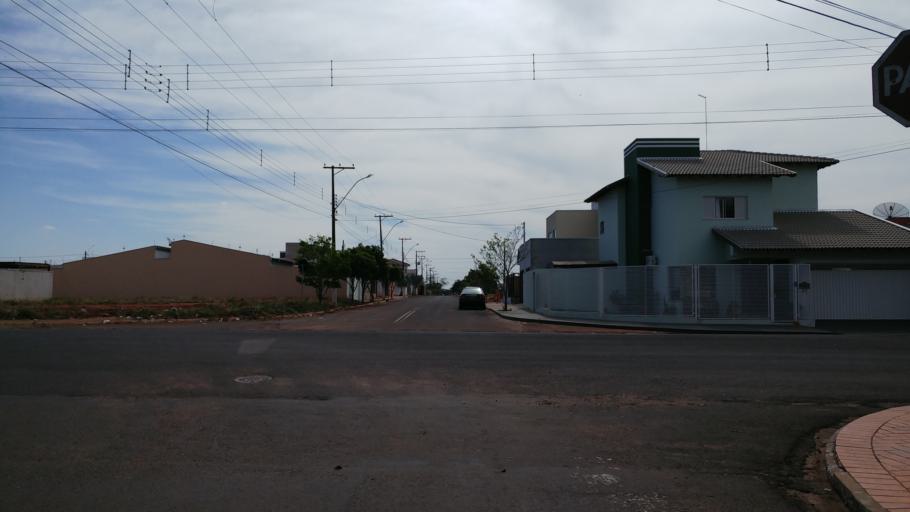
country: BR
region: Sao Paulo
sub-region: Paraguacu Paulista
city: Paraguacu Paulista
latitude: -22.4070
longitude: -50.5816
